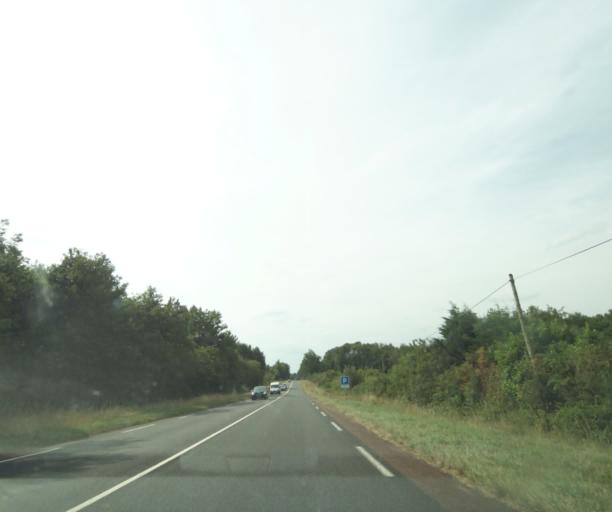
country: FR
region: Pays de la Loire
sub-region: Departement de la Sarthe
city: Marigne-Laille
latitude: 47.7971
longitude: 0.3316
